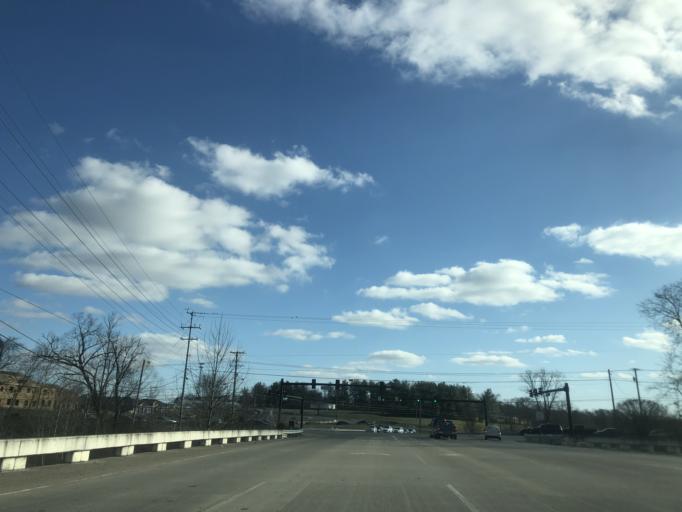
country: US
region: Tennessee
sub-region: Sumner County
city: Gallatin
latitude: 36.3469
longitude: -86.5253
